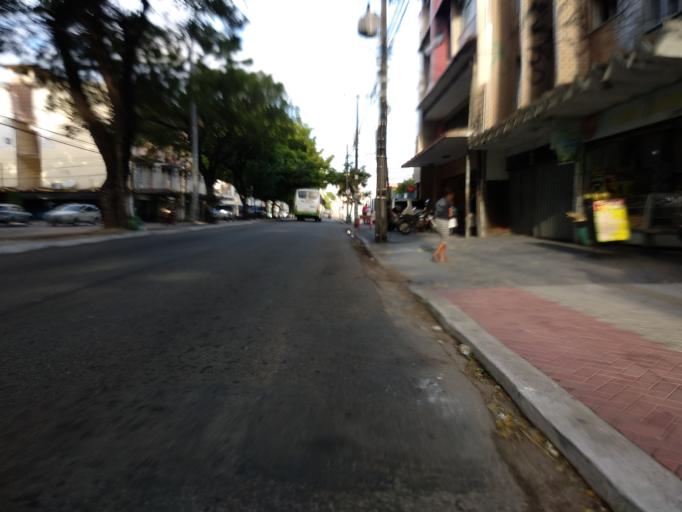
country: BR
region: Ceara
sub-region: Fortaleza
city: Fortaleza
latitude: -3.7328
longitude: -38.5266
